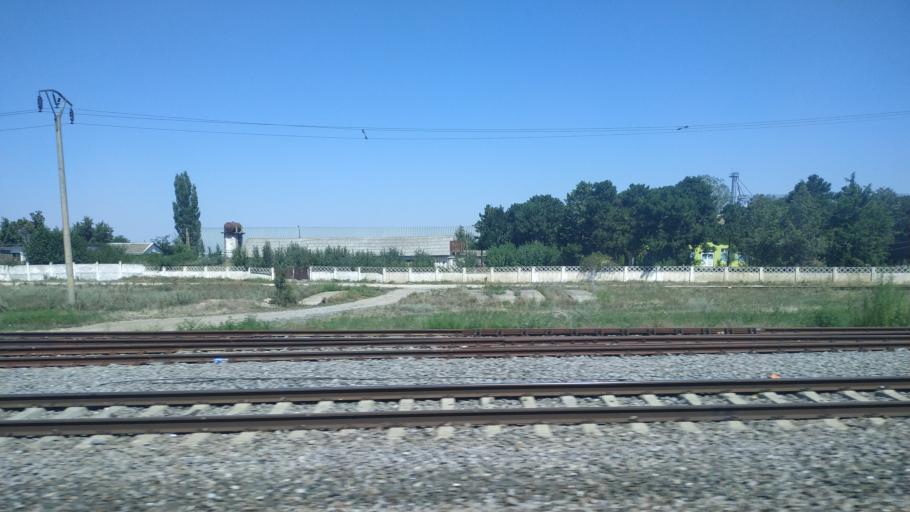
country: RO
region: Calarasi
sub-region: Comuna Borcea
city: Borcea
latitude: 44.4200
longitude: 27.7013
